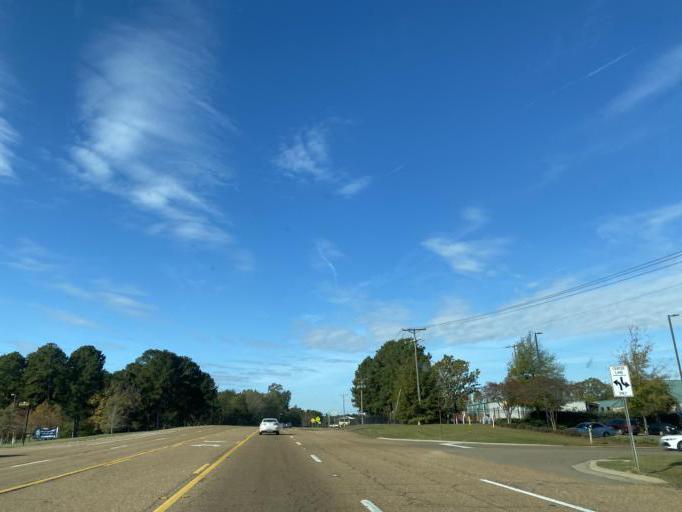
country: US
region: Mississippi
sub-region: Madison County
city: Madison
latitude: 32.4727
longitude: -90.1448
